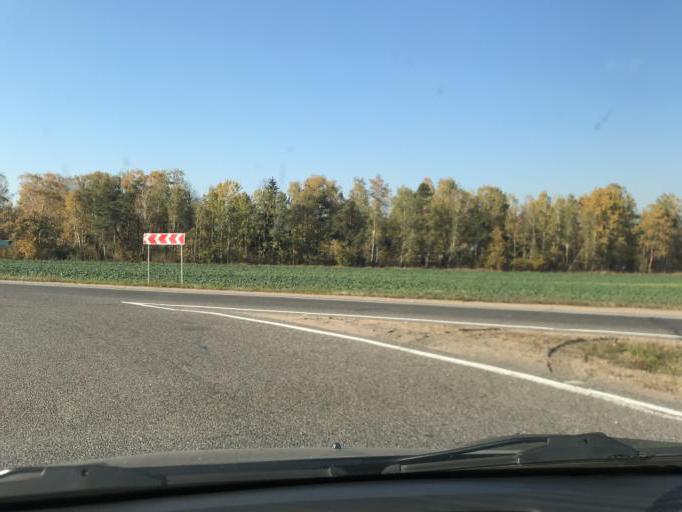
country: BY
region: Minsk
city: Pryvol'ny
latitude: 53.8064
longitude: 27.7966
